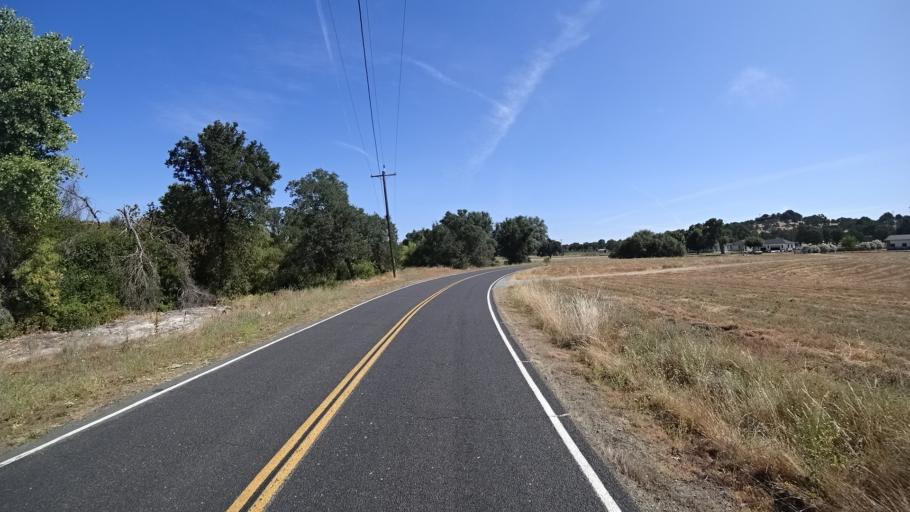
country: US
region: California
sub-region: Calaveras County
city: Rancho Calaveras
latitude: 38.1121
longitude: -120.9265
